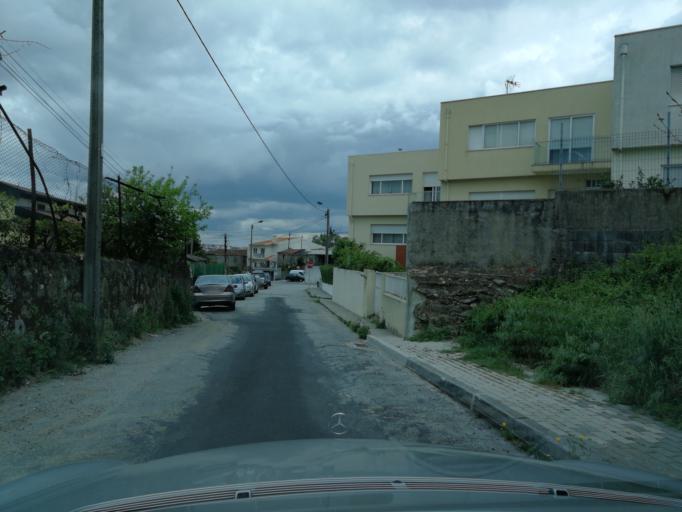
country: PT
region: Braga
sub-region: Braga
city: Braga
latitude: 41.5442
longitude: -8.3974
